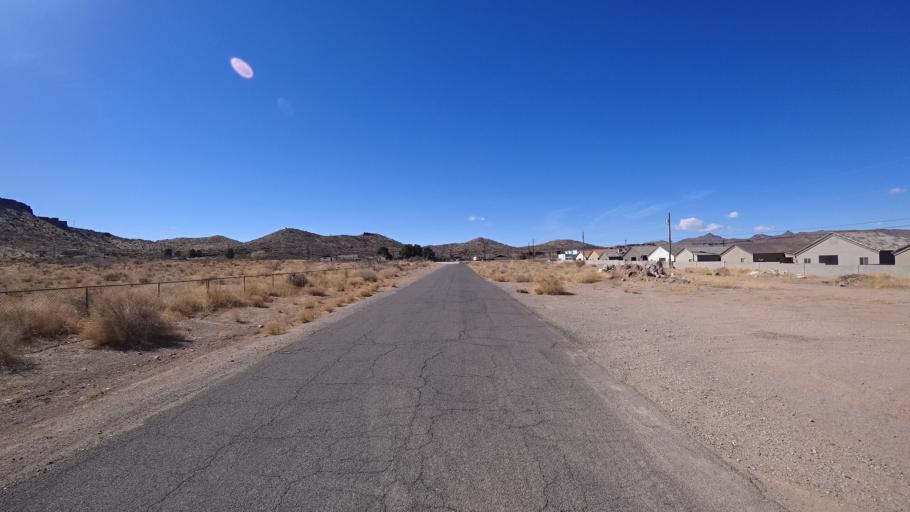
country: US
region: Arizona
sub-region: Mohave County
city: Kingman
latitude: 35.2031
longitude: -114.0381
